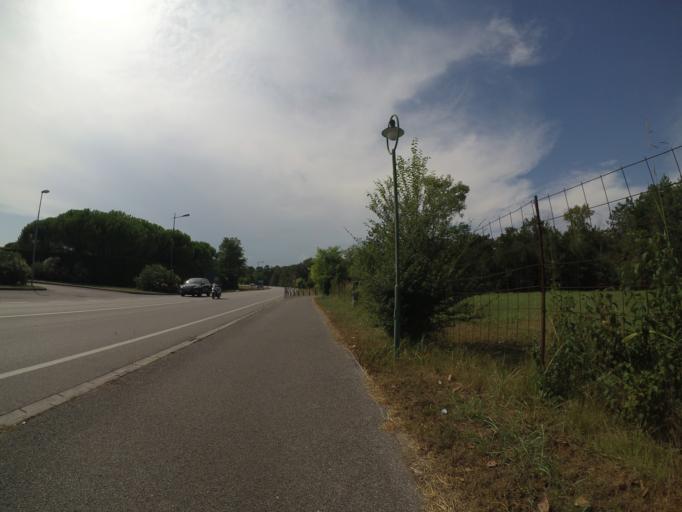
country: IT
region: Friuli Venezia Giulia
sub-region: Provincia di Udine
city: Lignano Sabbiadoro
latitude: 45.6625
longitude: 13.0853
